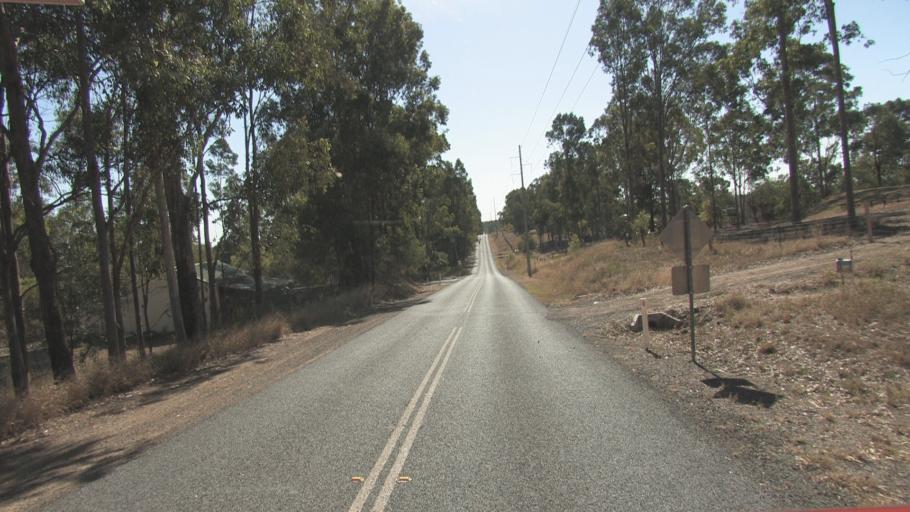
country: AU
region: Queensland
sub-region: Logan
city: Cedar Vale
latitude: -27.8805
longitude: 153.0157
